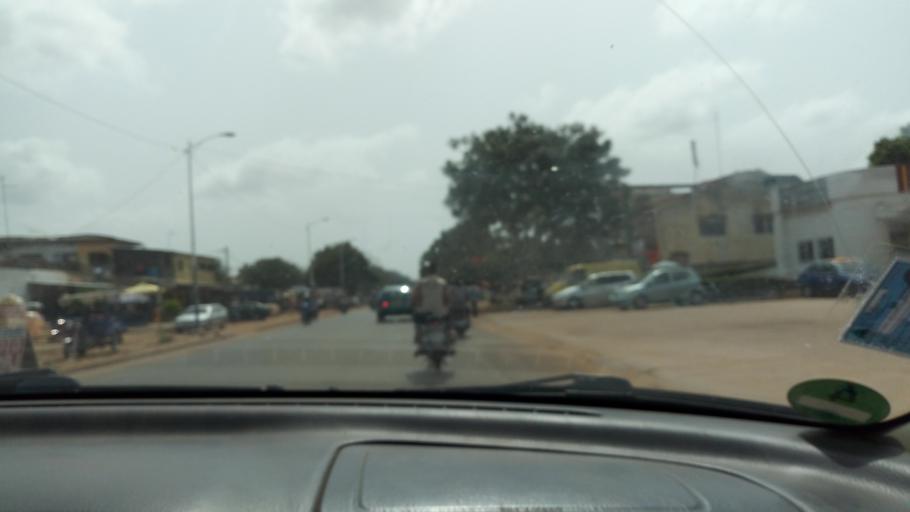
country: TG
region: Maritime
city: Lome
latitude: 6.1796
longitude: 1.1736
